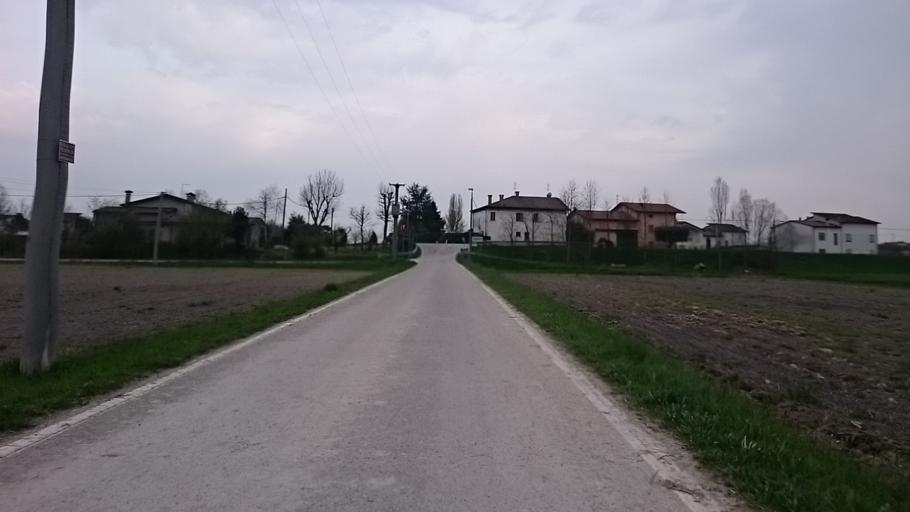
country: IT
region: Veneto
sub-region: Provincia di Padova
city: Tremignon
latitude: 45.5247
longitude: 11.8098
